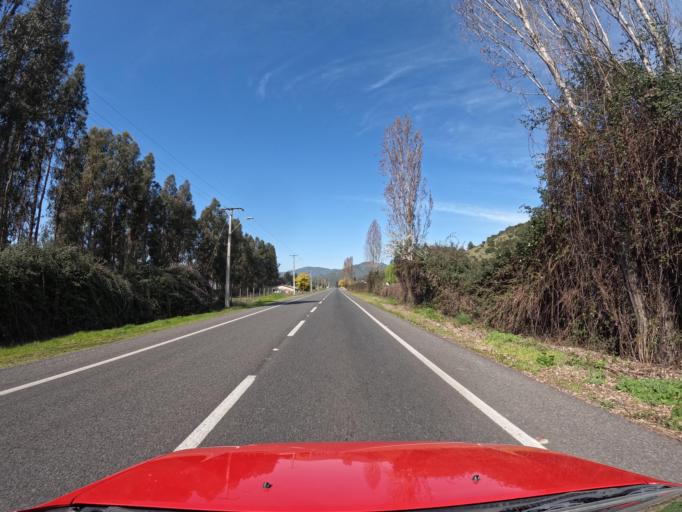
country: CL
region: Maule
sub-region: Provincia de Curico
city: Teno
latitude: -34.9783
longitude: -70.9640
